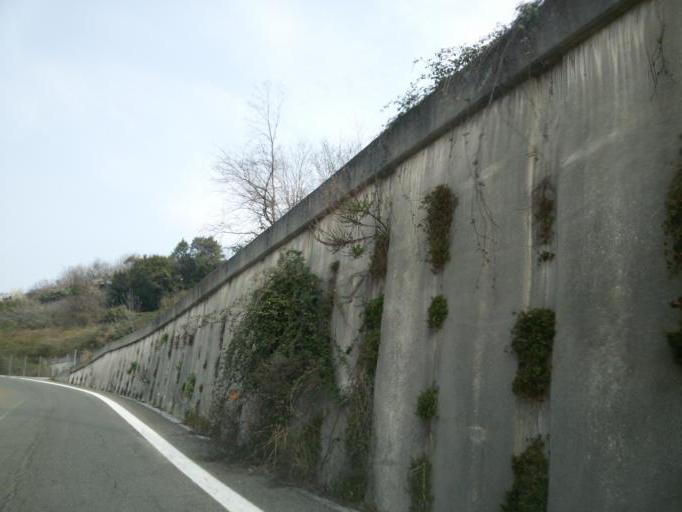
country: IT
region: Liguria
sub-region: Provincia di Genova
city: San Teodoro
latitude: 44.4217
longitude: 8.8683
